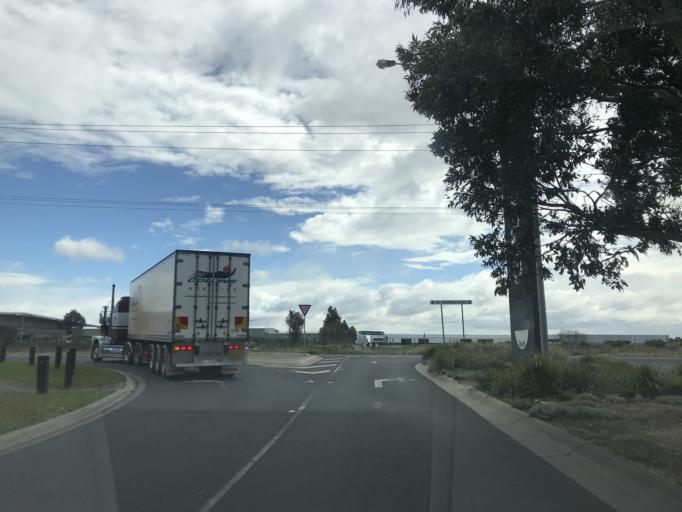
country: AU
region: Victoria
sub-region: Brimbank
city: Derrimut
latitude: -37.8024
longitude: 144.7710
